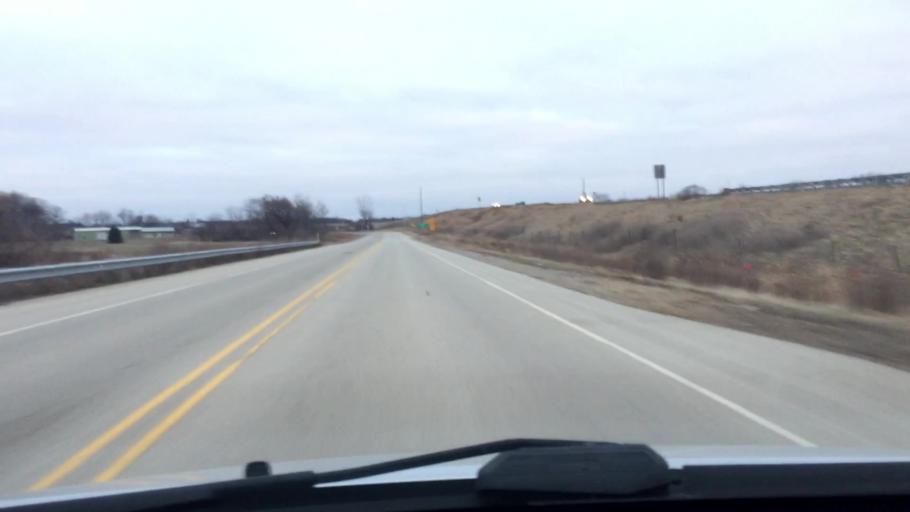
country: US
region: Wisconsin
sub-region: Jefferson County
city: Watertown
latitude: 43.1597
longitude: -88.7529
